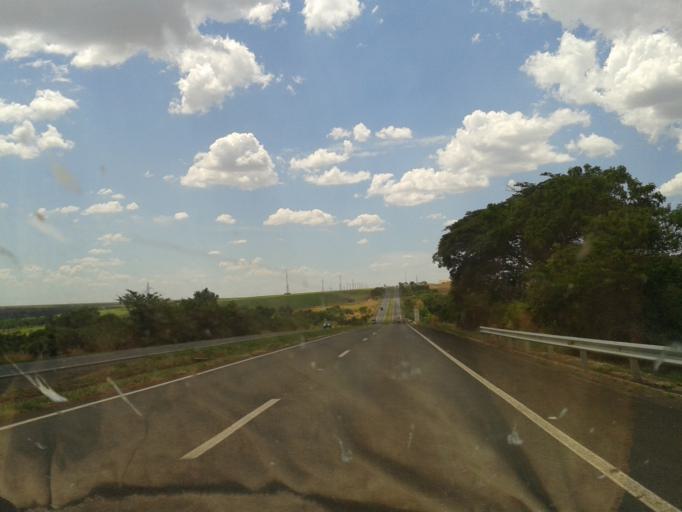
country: BR
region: Minas Gerais
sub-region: Uberlandia
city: Uberlandia
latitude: -19.0934
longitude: -48.1834
